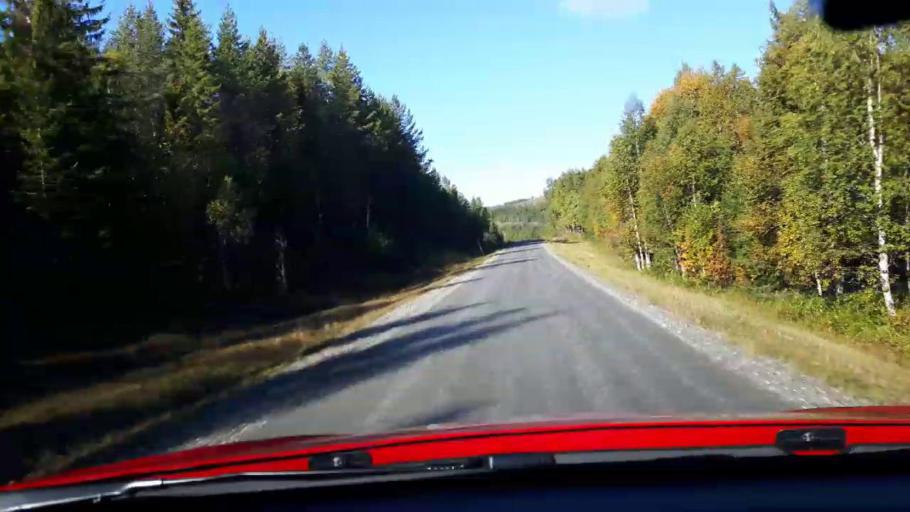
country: NO
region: Nord-Trondelag
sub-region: Lierne
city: Sandvika
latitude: 64.5875
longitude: 13.8683
